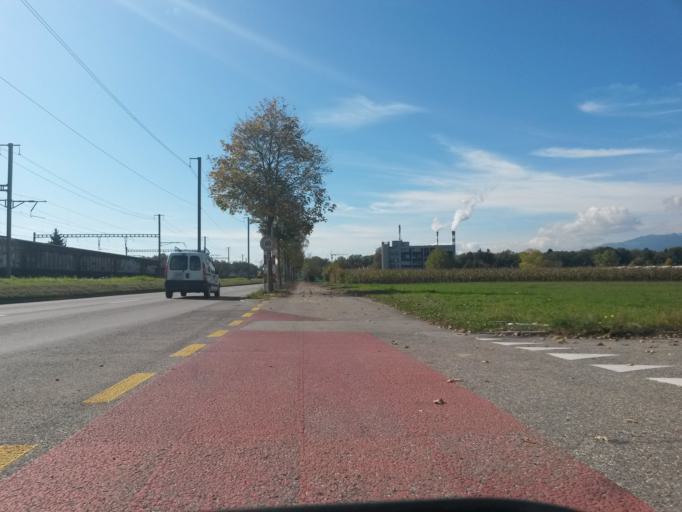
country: CH
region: Solothurn
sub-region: Bezirk Wasseramt
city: Luterbach
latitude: 47.2170
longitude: 7.5818
